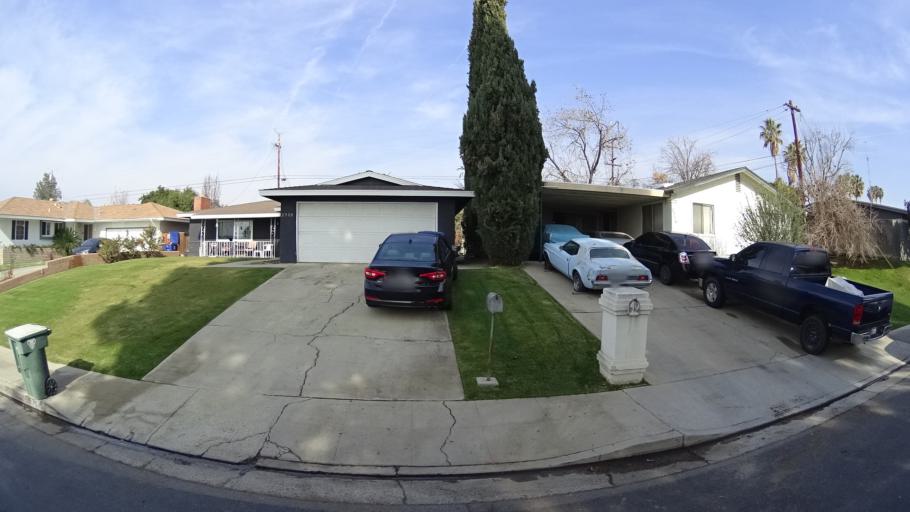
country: US
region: California
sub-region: Kern County
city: Oildale
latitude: 35.4058
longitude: -118.9623
